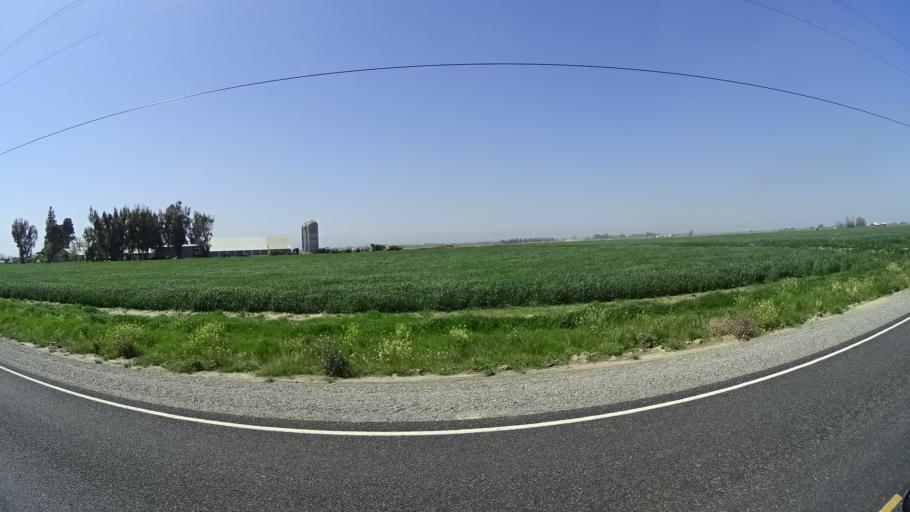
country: US
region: California
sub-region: Glenn County
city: Willows
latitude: 39.5348
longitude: -122.1365
